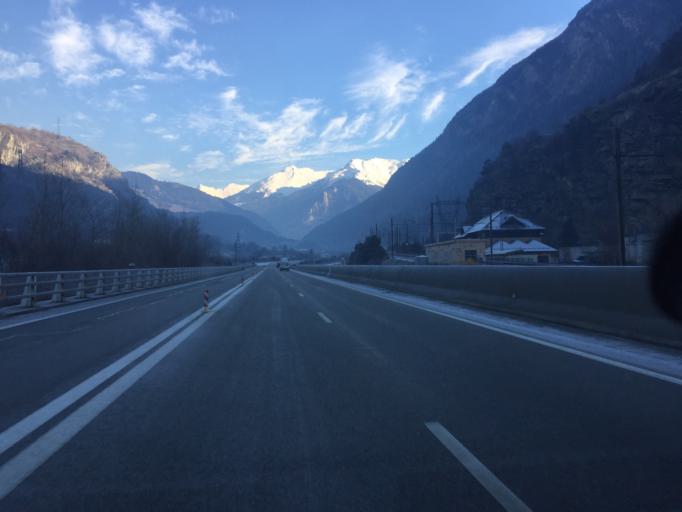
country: FR
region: Rhone-Alpes
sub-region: Departement de la Savoie
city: Modane
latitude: 45.2058
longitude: 6.5763
